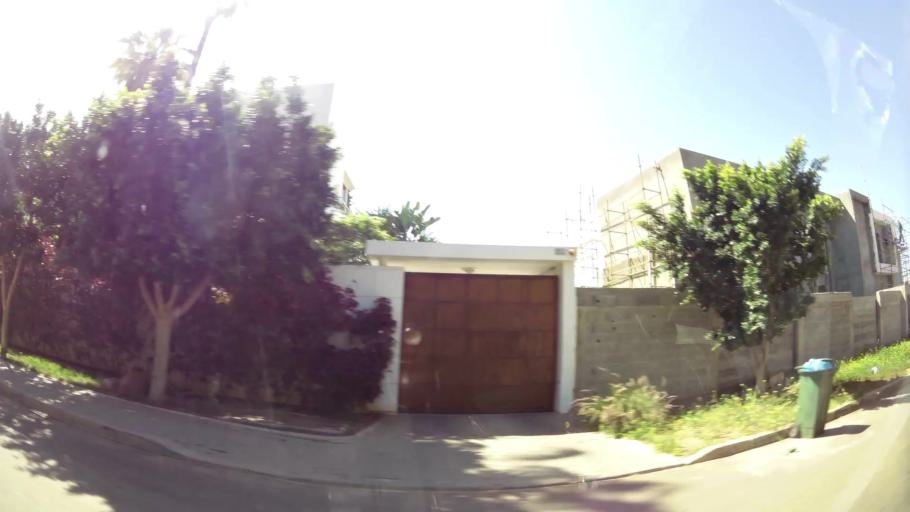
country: MA
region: Souss-Massa-Draa
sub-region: Agadir-Ida-ou-Tnan
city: Agadir
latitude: 30.4419
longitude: -9.5884
